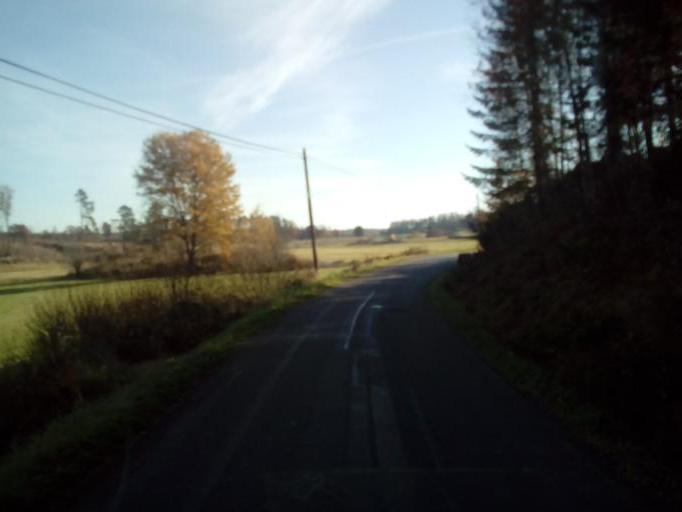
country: SE
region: Kalmar
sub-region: Vasterviks Kommun
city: Ankarsrum
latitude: 57.8005
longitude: 16.1771
